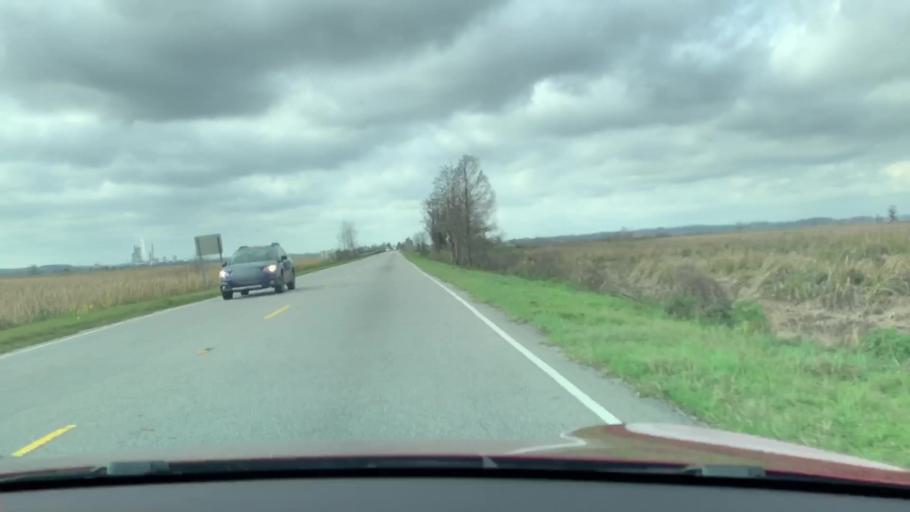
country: US
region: Georgia
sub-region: Chatham County
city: Port Wentworth
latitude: 32.1660
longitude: -81.1223
